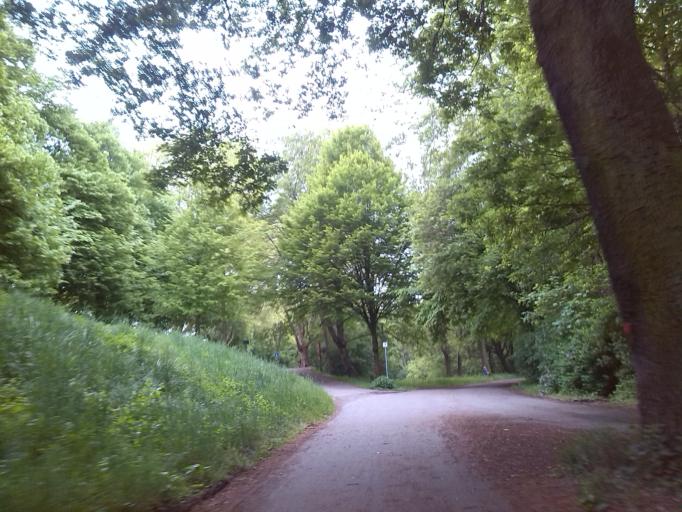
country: DE
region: Rheinland-Pfalz
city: Ludwigshafen am Rhein
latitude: 49.4657
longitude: 8.4652
